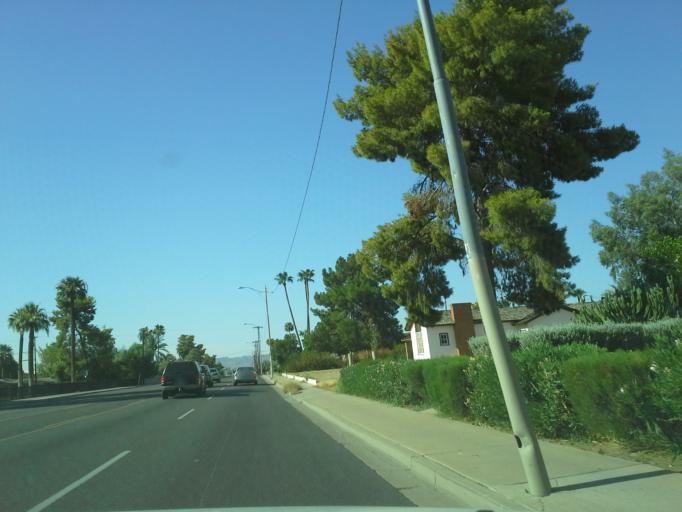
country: US
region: Arizona
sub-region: Maricopa County
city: Phoenix
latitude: 33.4782
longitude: -112.1001
